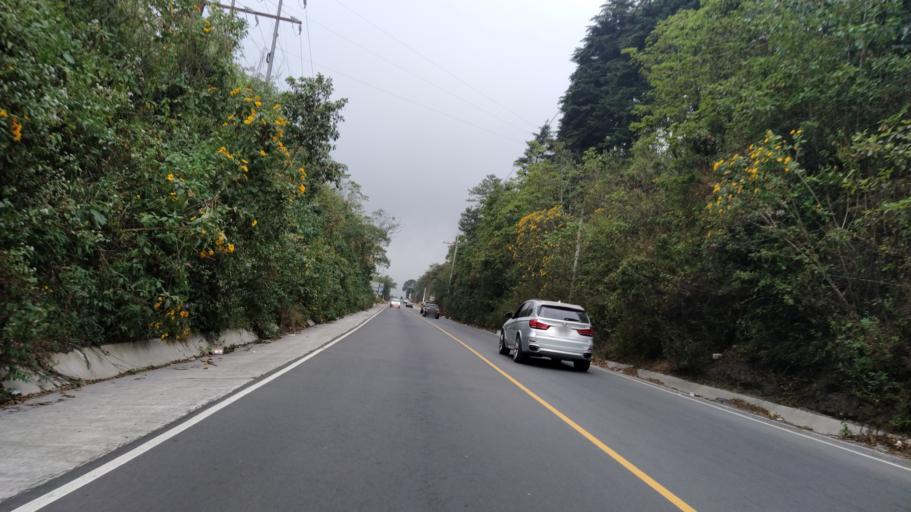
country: GT
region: Quetzaltenango
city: Zunil
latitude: 14.7385
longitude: -91.5201
